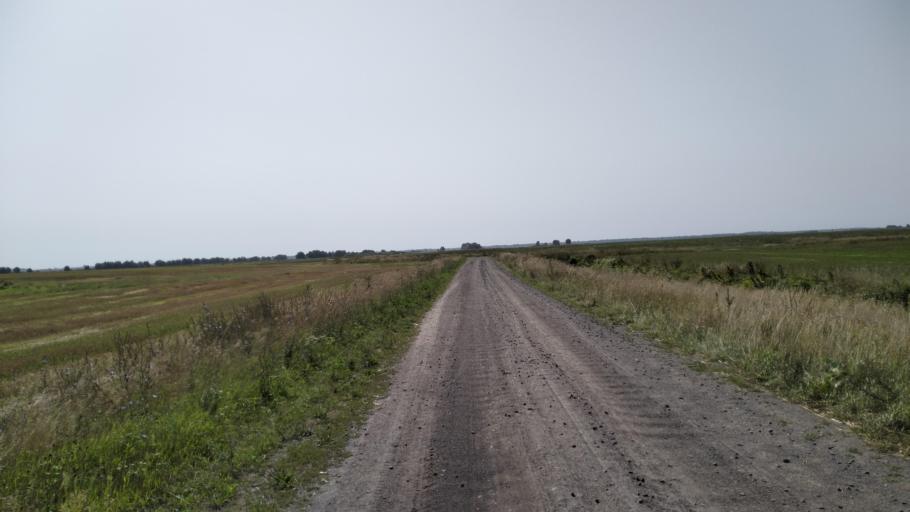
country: BY
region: Brest
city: Davyd-Haradok
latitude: 52.0099
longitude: 27.1659
